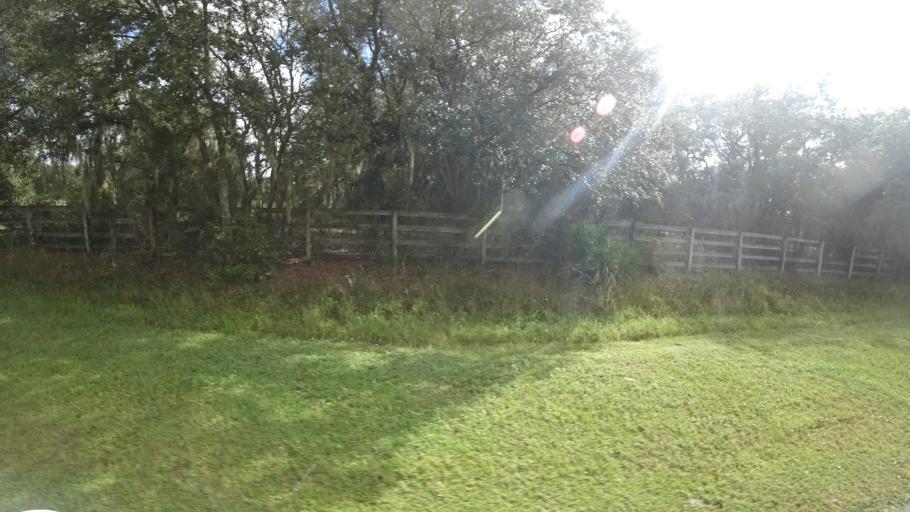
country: US
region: Florida
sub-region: Sarasota County
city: Lake Sarasota
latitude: 27.3620
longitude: -82.2510
